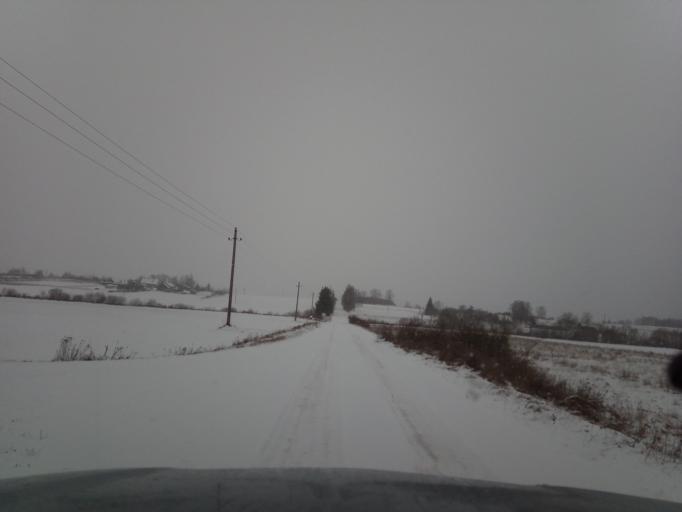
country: LT
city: Ramygala
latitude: 55.5894
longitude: 24.3533
